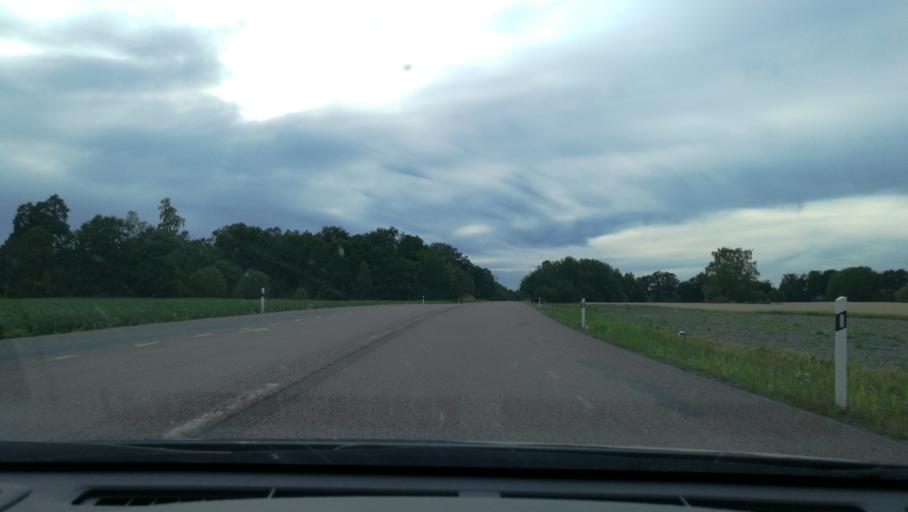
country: SE
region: Vaestmanland
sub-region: Kungsors Kommun
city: Kungsoer
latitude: 59.4336
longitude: 16.0688
